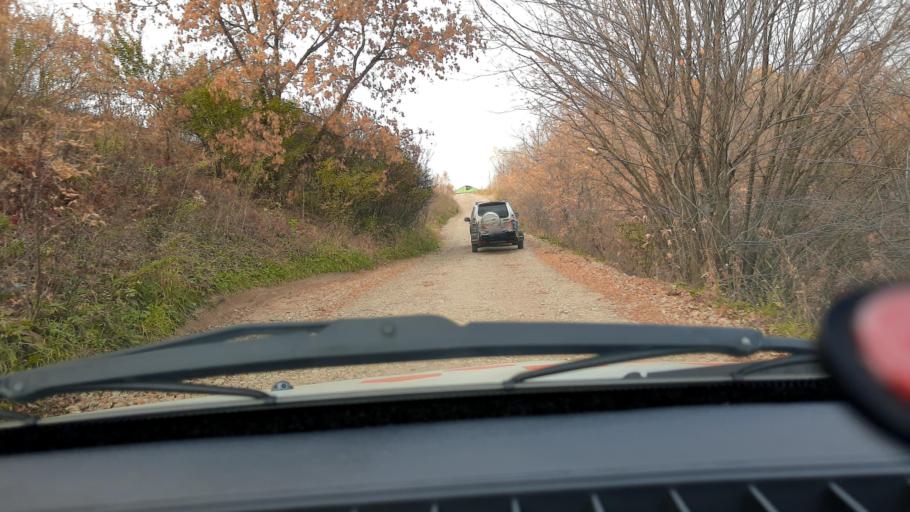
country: RU
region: Bashkortostan
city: Iglino
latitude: 54.7933
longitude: 56.3339
